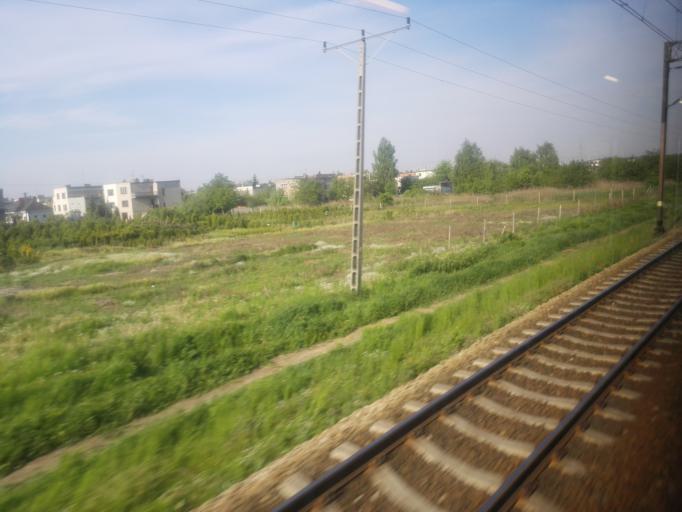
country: PL
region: Greater Poland Voivodeship
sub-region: Powiat wrzesinski
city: Wrzesnia
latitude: 52.3375
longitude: 17.5810
